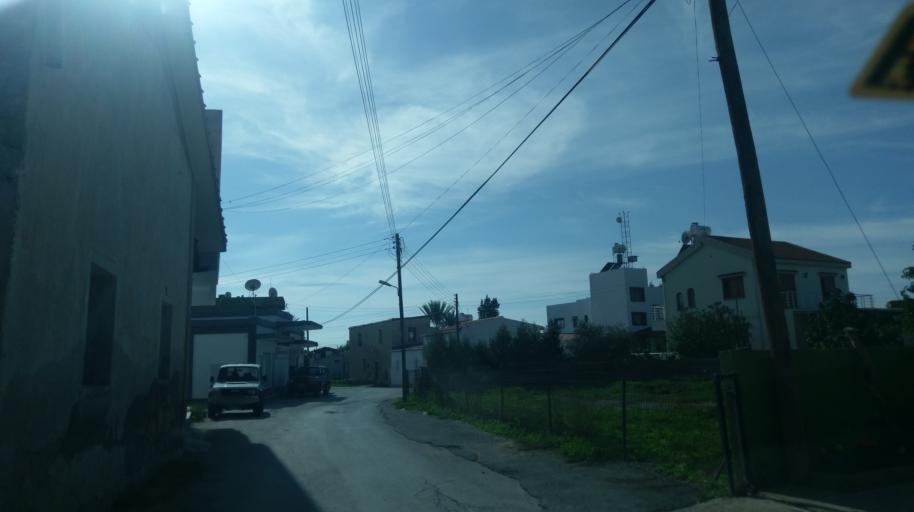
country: CY
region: Ammochostos
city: Lefkonoiko
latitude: 35.2564
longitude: 33.6025
